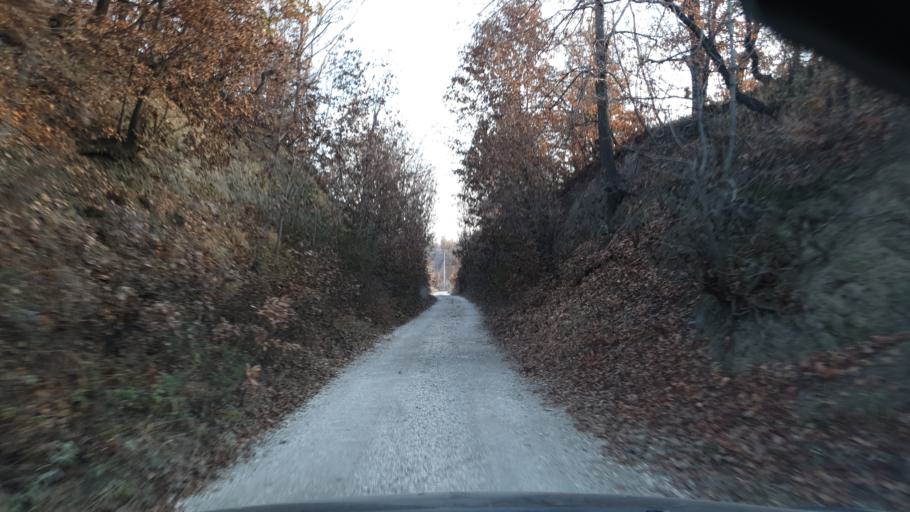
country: RS
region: Central Serbia
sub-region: Borski Okrug
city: Bor
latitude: 44.0628
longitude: 22.0812
